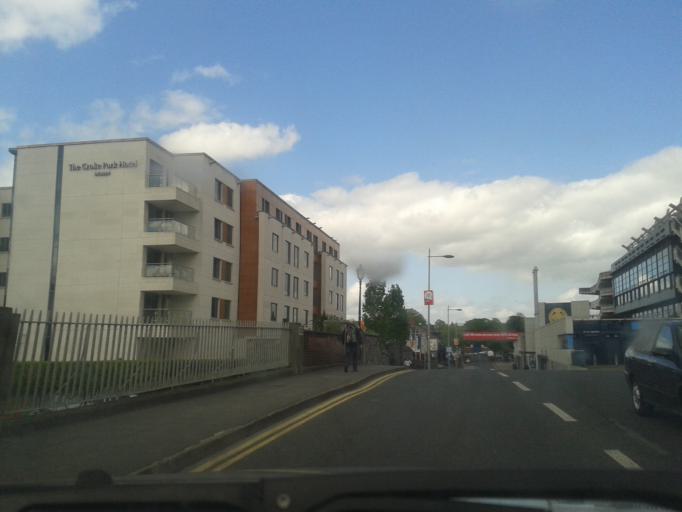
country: IE
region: Leinster
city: Drumcondra
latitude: 53.3600
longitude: -6.2538
